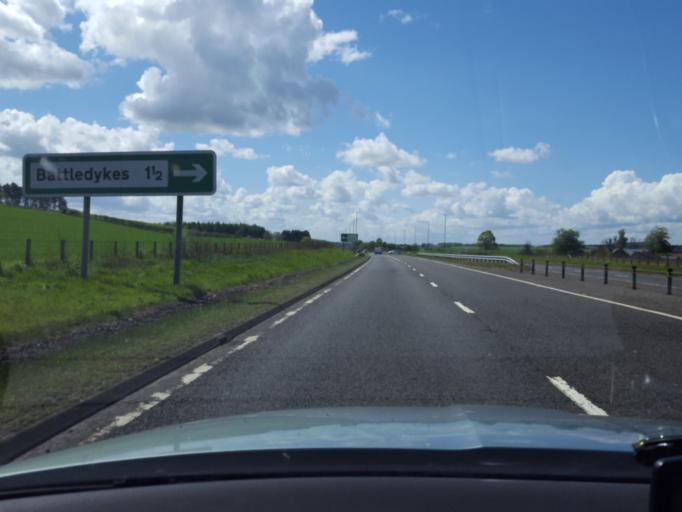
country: GB
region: Scotland
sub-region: Angus
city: Forfar
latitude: 56.6742
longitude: -2.8925
